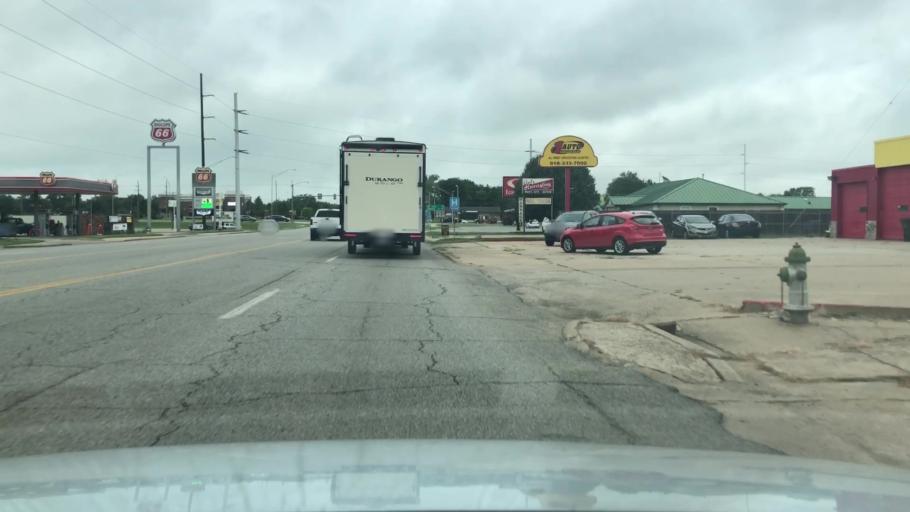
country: US
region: Oklahoma
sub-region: Washington County
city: Bartlesville
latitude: 36.7281
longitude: -95.9326
